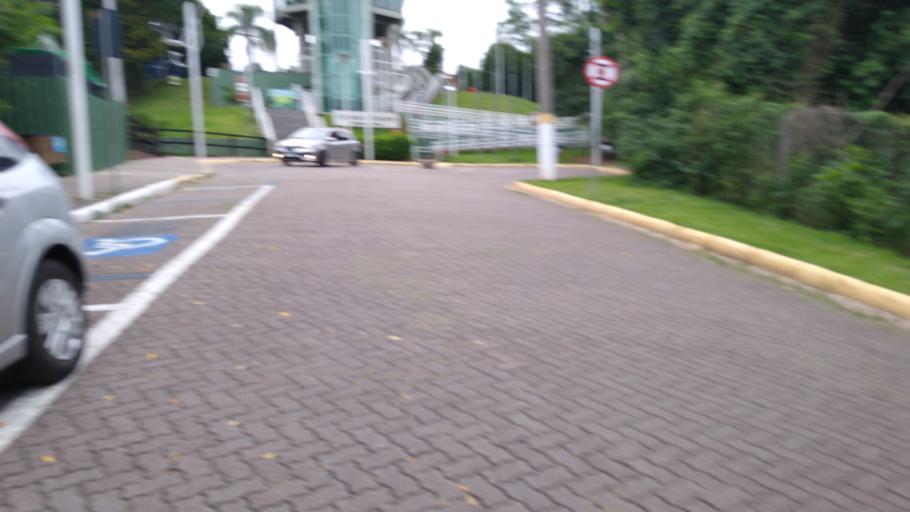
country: BR
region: Santa Catarina
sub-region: Itapema
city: Itapema
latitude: -27.0878
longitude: -48.6031
